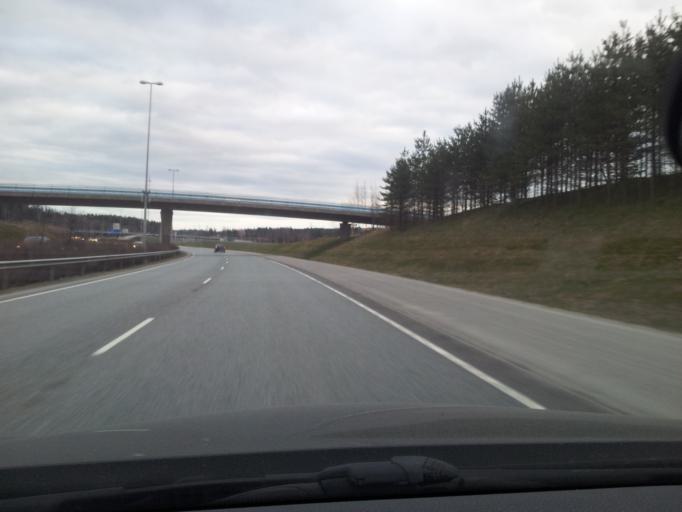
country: FI
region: Uusimaa
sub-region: Helsinki
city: Kauniainen
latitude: 60.1941
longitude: 24.7433
